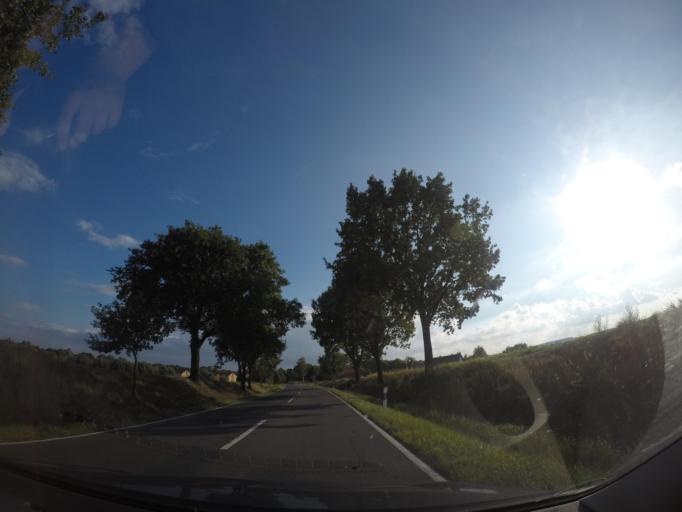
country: DE
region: Saxony-Anhalt
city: Weferlingen
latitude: 52.3506
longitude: 11.0778
